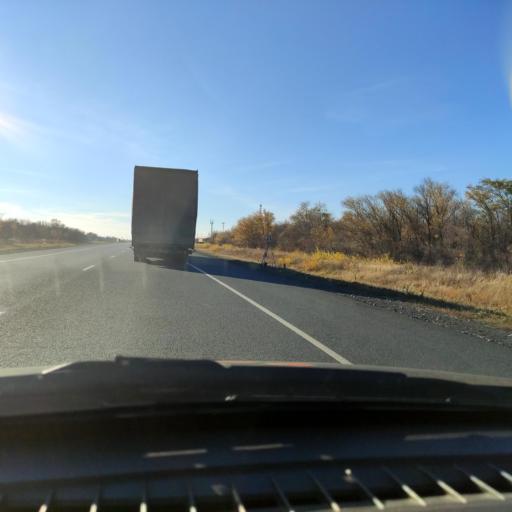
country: RU
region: Samara
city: Obsharovka
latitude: 53.2241
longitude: 48.8748
